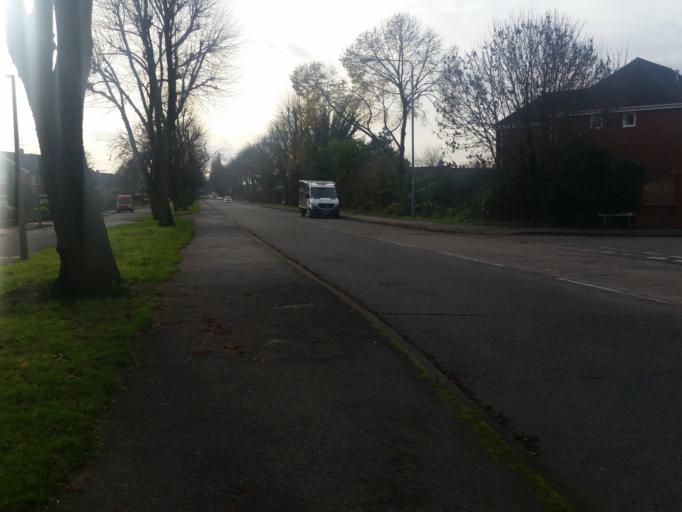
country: GB
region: England
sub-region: Derbyshire
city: Long Eaton
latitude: 52.9182
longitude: -1.2297
